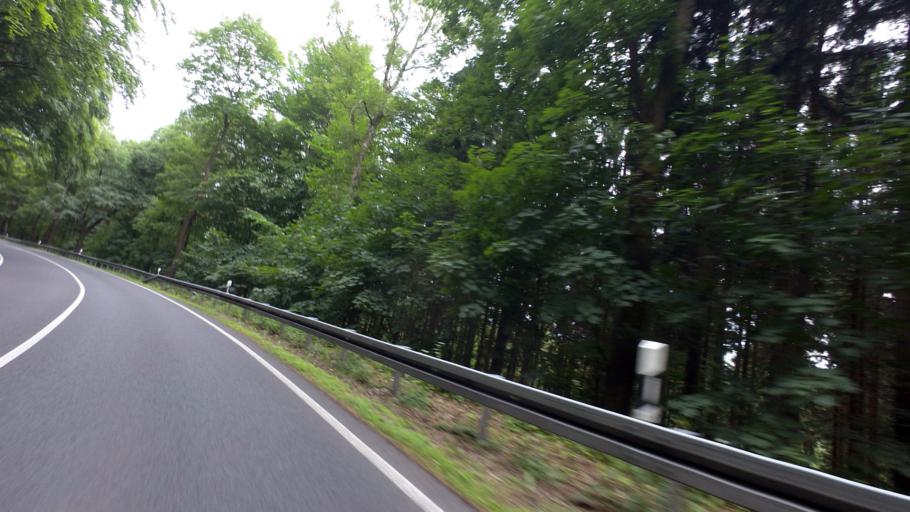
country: DE
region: Saxony
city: Sebnitz
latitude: 50.9888
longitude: 14.2407
